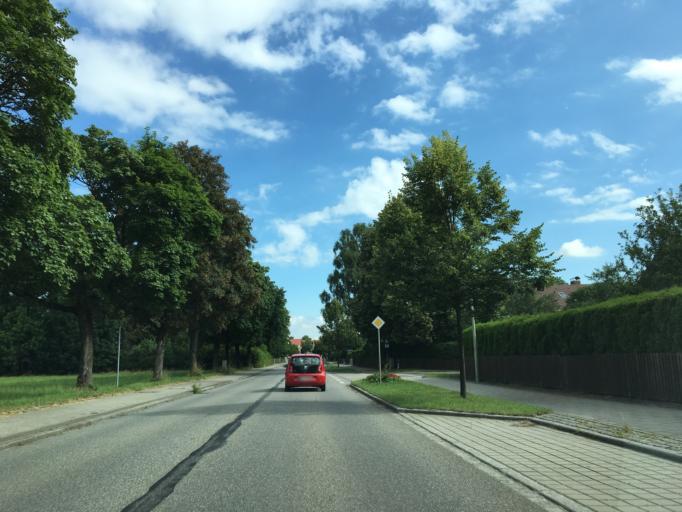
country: DE
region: Bavaria
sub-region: Upper Bavaria
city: Sauerlach
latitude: 47.9681
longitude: 11.6536
